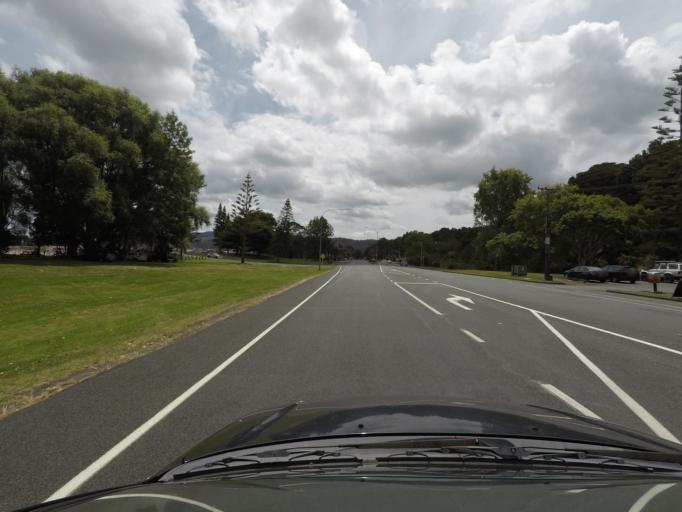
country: NZ
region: Northland
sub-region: Whangarei
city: Whangarei
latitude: -35.7290
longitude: 174.3379
